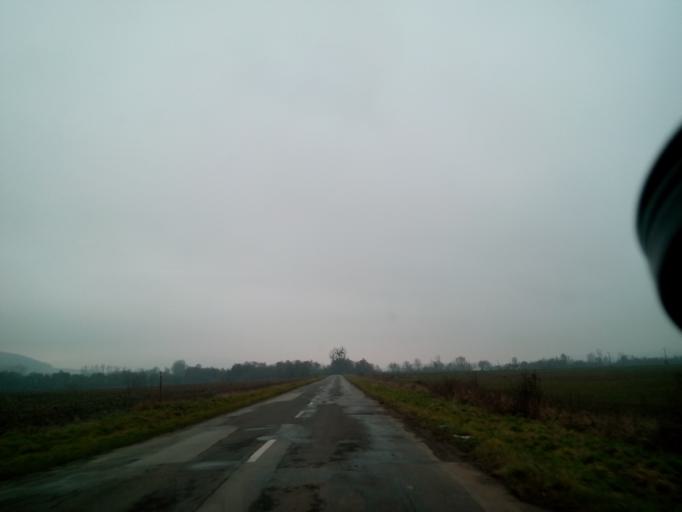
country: SK
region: Kosicky
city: Kosice
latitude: 48.7263
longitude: 21.4383
